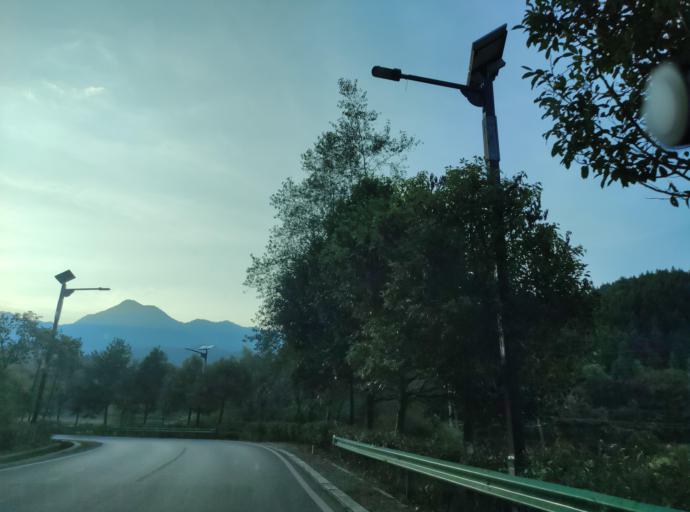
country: CN
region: Jiangxi Sheng
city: Zhangjiafang
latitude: 27.5282
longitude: 114.0261
